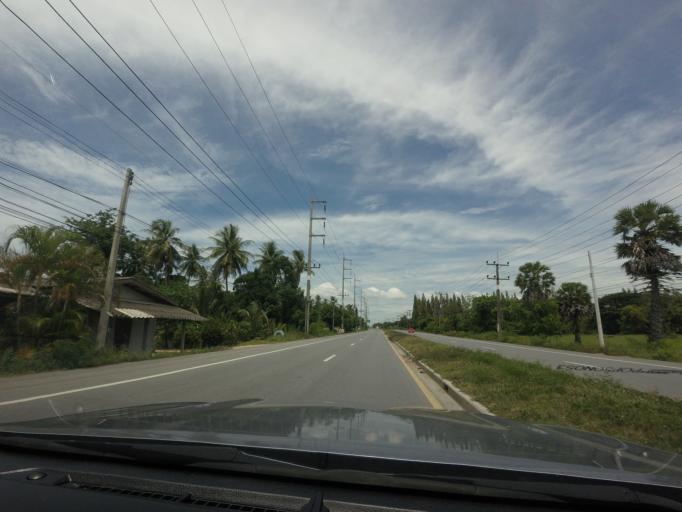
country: TH
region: Songkhla
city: Ranot
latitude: 7.7087
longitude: 100.3731
